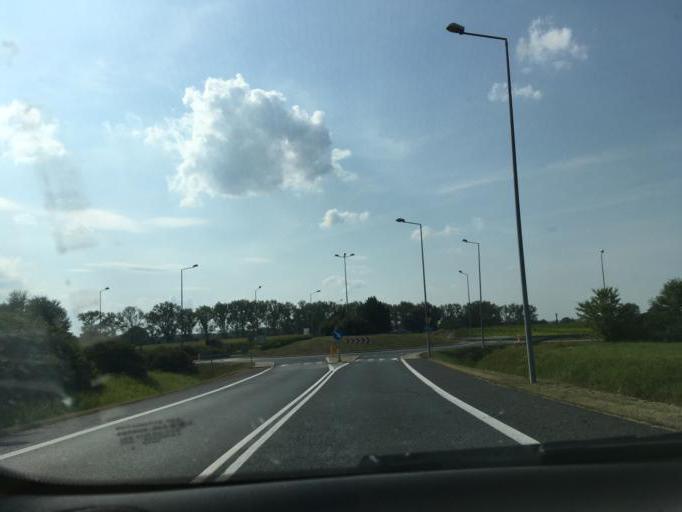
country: PL
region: Opole Voivodeship
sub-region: Powiat prudnicki
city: Prudnik
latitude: 50.3364
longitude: 17.5696
